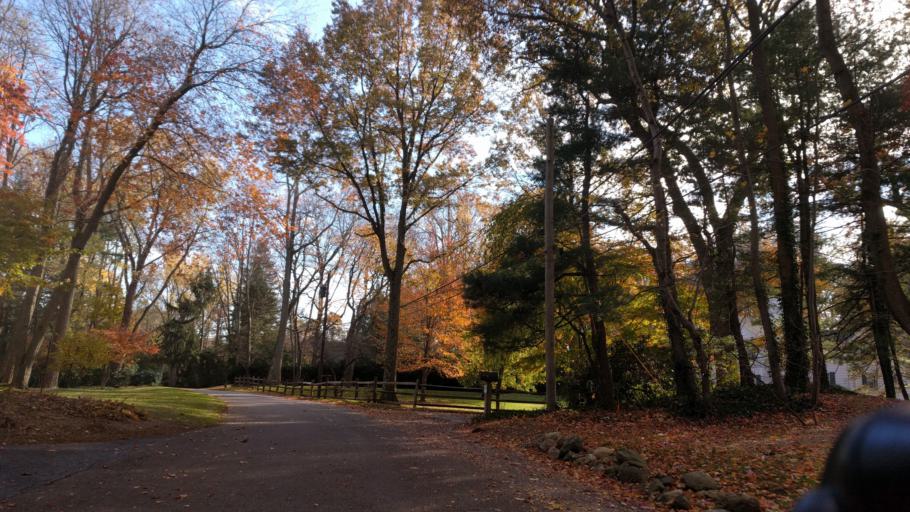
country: US
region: New York
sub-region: Nassau County
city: Locust Valley
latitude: 40.8743
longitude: -73.5820
